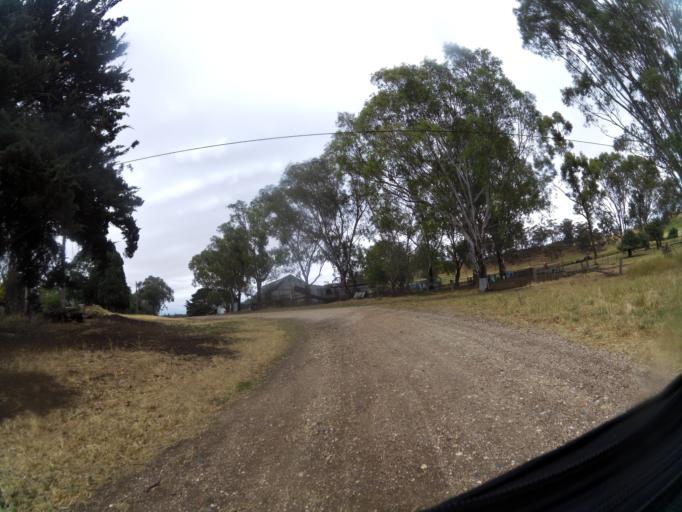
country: AU
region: Victoria
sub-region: Mount Alexander
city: Castlemaine
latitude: -37.2001
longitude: 144.0150
